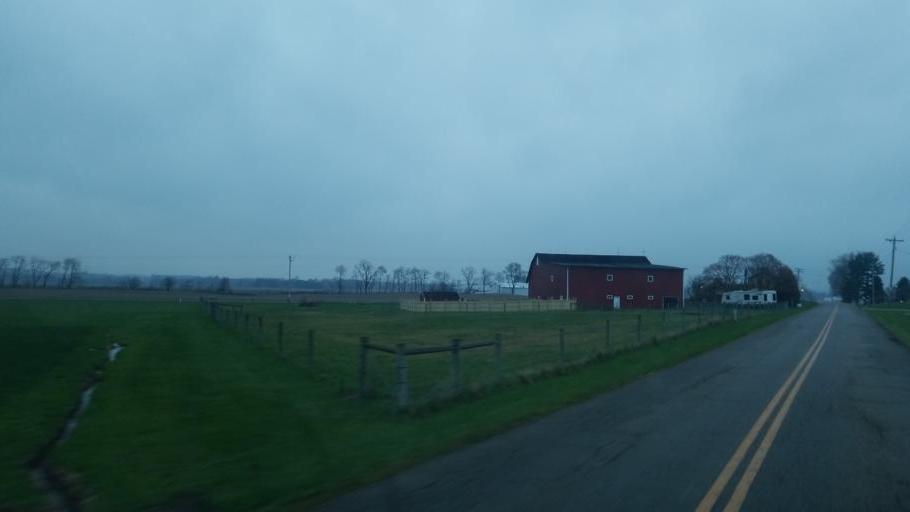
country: US
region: Ohio
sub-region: Knox County
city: Fredericktown
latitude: 40.4496
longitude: -82.5790
